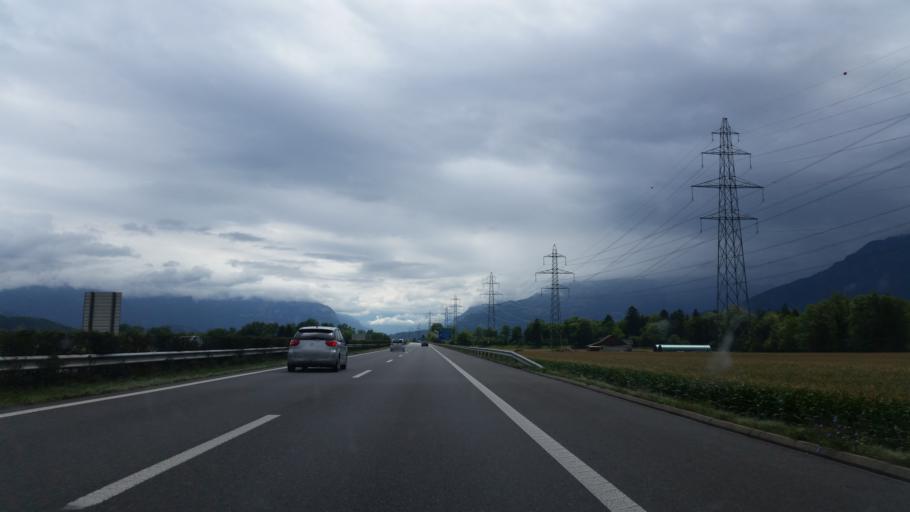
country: CH
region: Vaud
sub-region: Aigle District
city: Aigle
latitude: 46.3294
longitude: 6.9353
